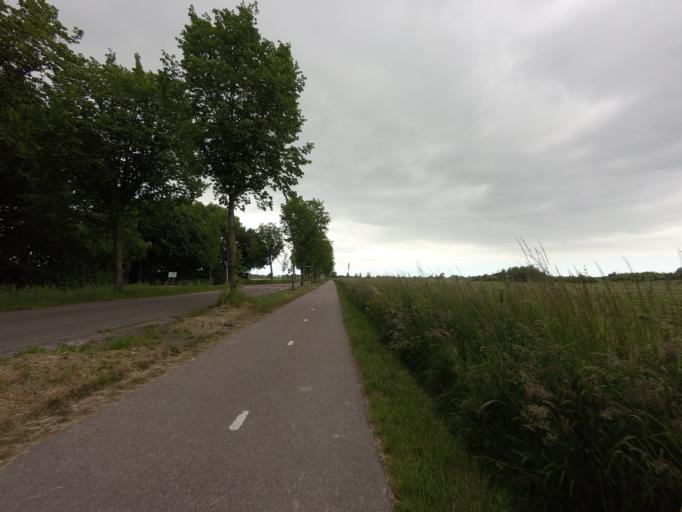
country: NL
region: North Holland
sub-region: Gemeente Hoorn
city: Hoorn
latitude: 52.6453
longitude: 5.0029
